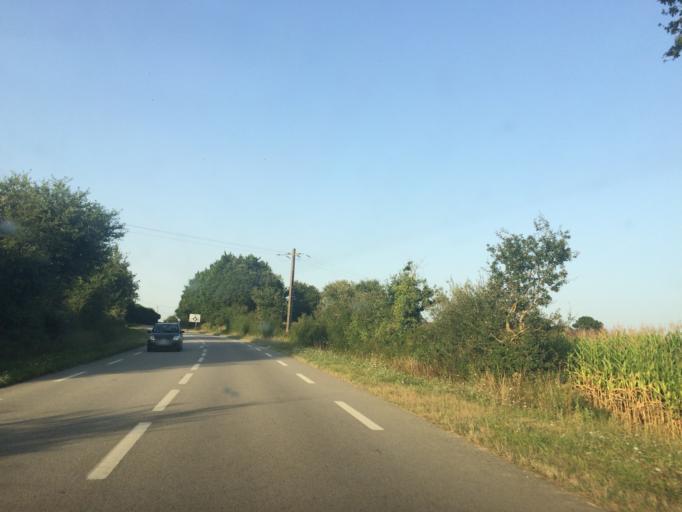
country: FR
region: Brittany
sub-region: Departement du Morbihan
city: Ambon
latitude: 47.5343
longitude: -2.5474
